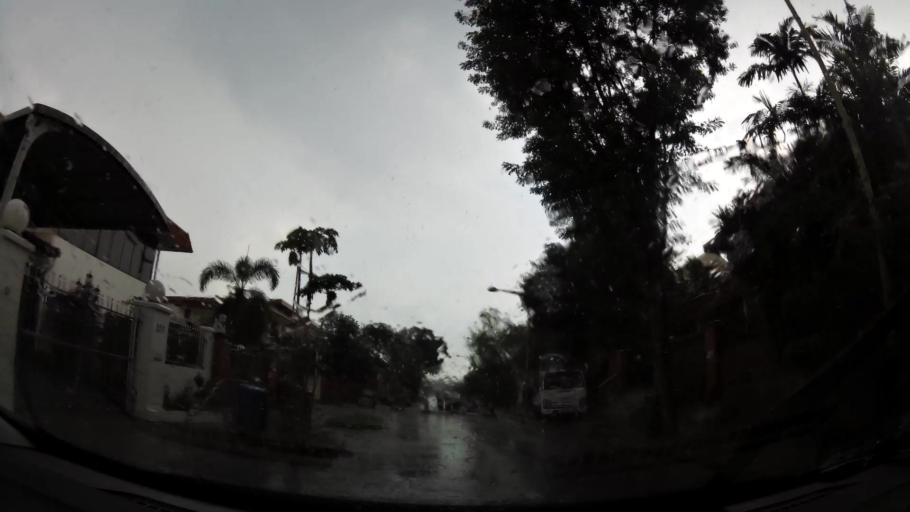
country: SG
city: Singapore
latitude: 1.3325
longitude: 103.9485
